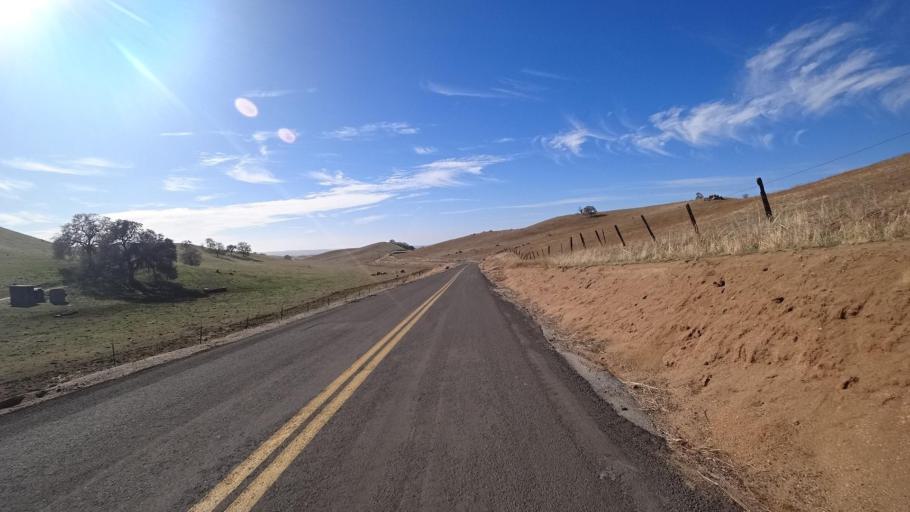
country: US
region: California
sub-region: Tulare County
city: Richgrove
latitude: 35.6921
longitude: -118.8709
